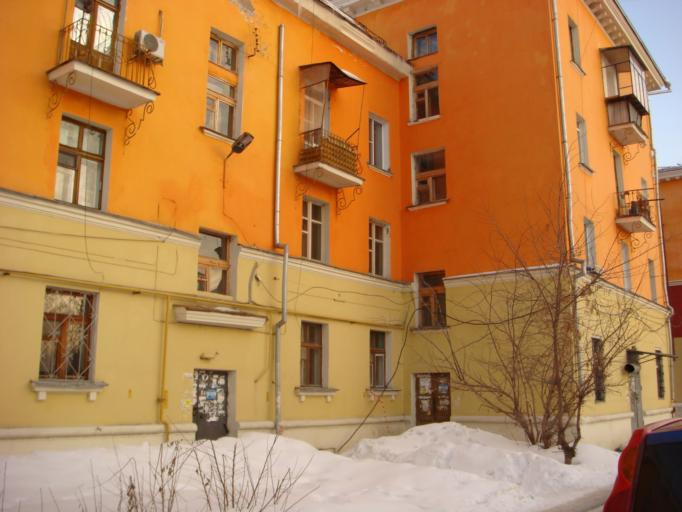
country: RU
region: Chelyabinsk
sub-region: Gorod Chelyabinsk
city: Chelyabinsk
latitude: 55.1194
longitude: 61.4708
